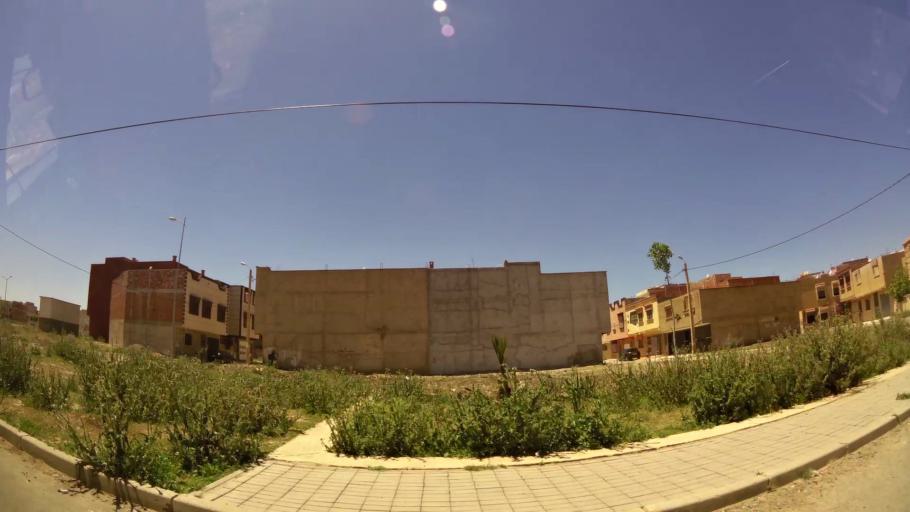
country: MA
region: Oriental
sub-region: Oujda-Angad
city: Oujda
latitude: 34.6760
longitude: -1.8653
